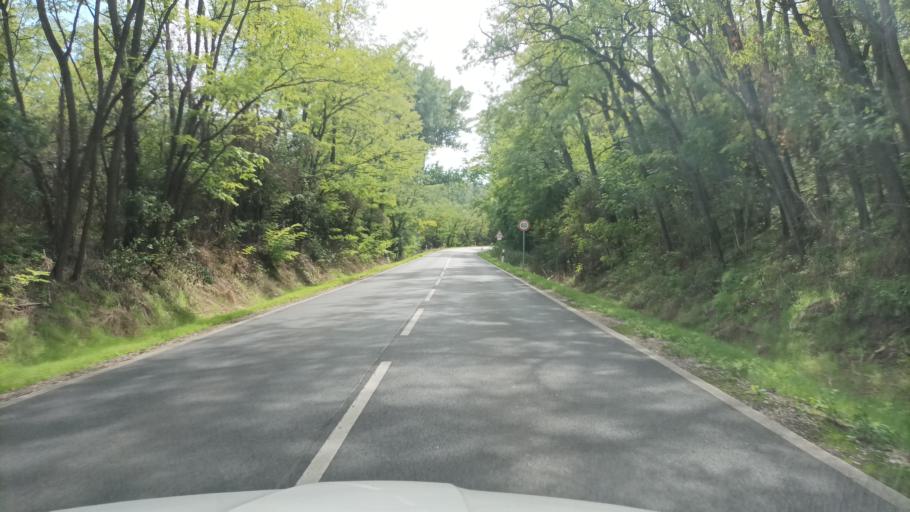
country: HU
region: Pest
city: Pecel
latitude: 47.5051
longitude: 19.3712
